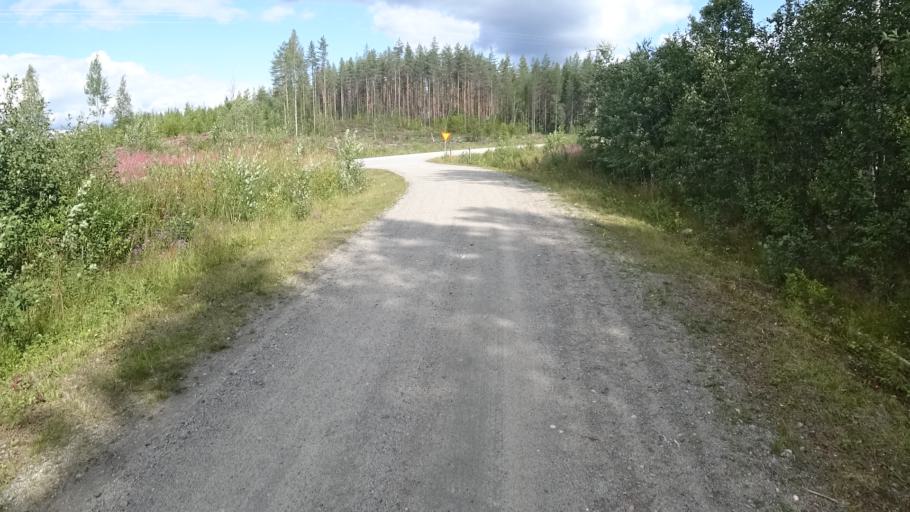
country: FI
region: North Karelia
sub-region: Joensuu
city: Ilomantsi
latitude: 62.6246
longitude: 31.2519
